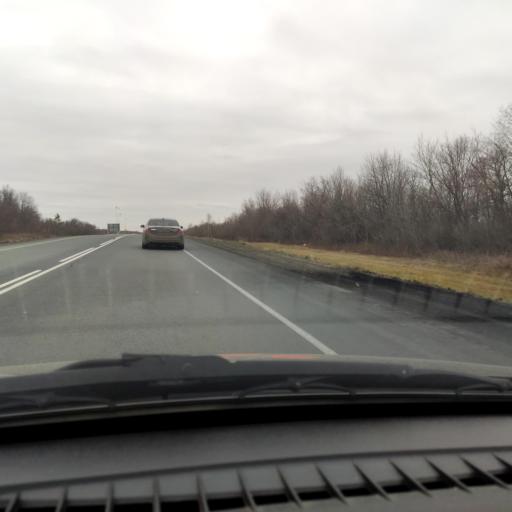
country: RU
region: Samara
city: Zhigulevsk
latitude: 53.3501
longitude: 49.4523
